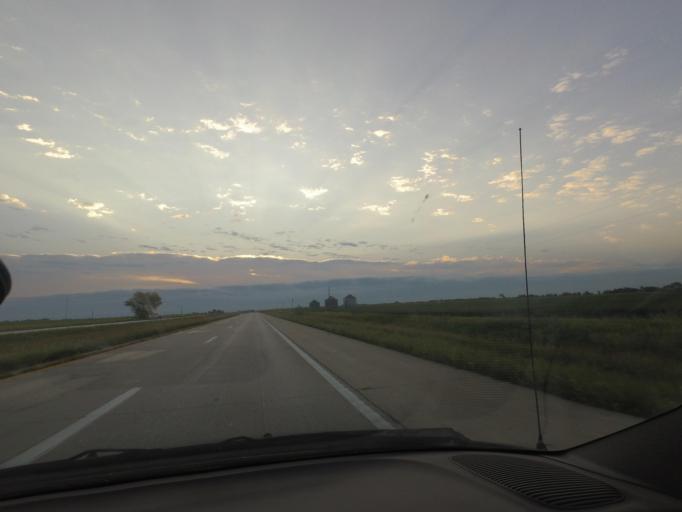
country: US
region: Missouri
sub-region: Macon County
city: Macon
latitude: 39.7498
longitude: -92.3030
